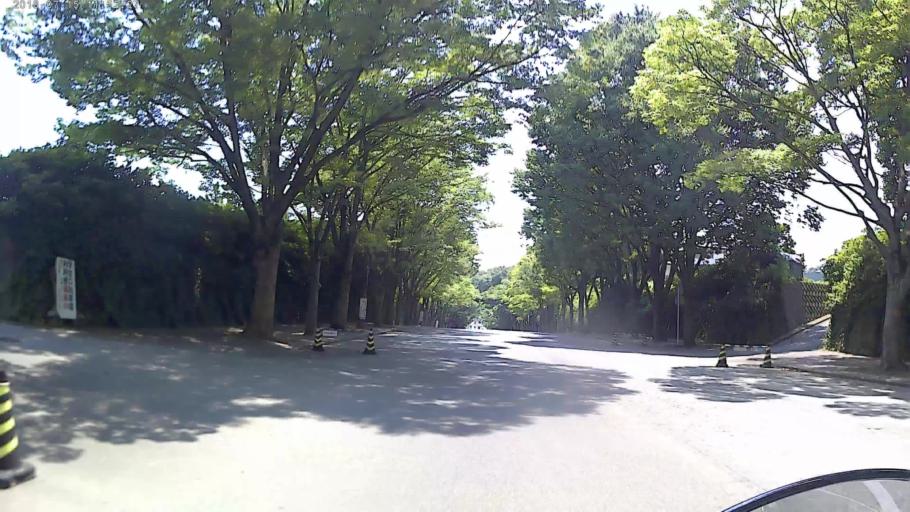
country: JP
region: Kanagawa
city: Isehara
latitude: 35.3597
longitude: 139.2733
